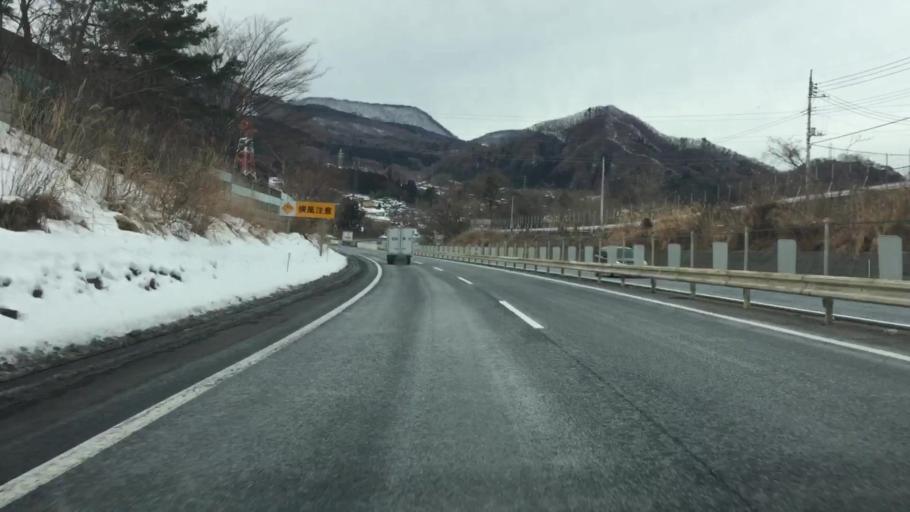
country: JP
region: Gunma
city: Numata
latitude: 36.7087
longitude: 138.9819
